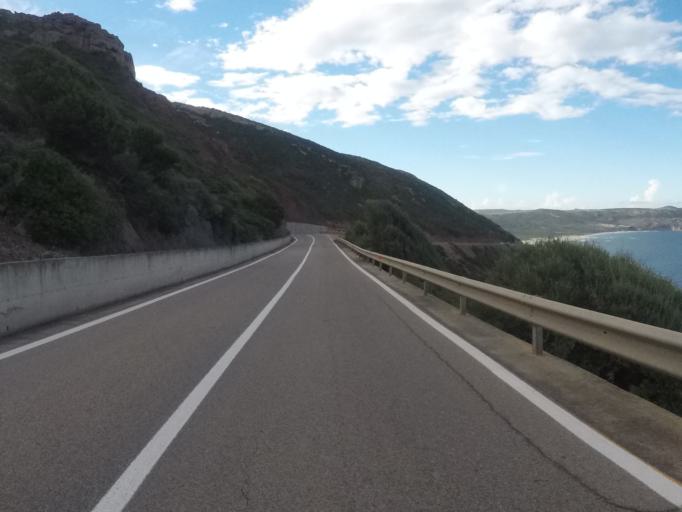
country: IT
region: Sardinia
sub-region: Provincia di Carbonia-Iglesias
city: Gonnesa
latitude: 39.3045
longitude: 8.4362
